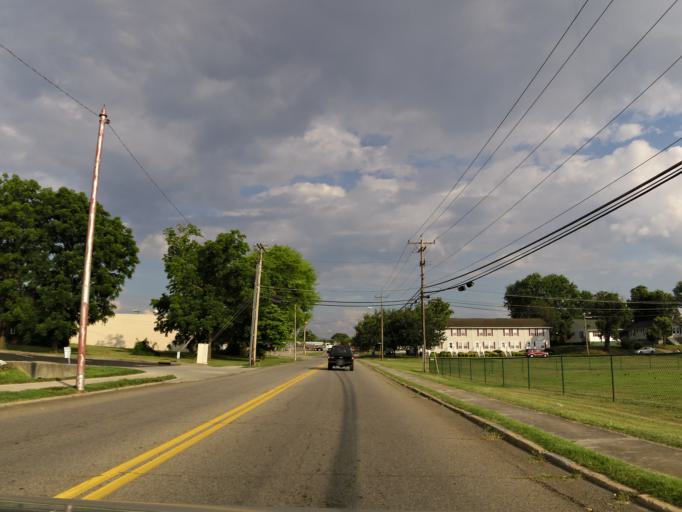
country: US
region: Tennessee
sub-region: Blount County
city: Maryville
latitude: 35.7676
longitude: -83.9758
